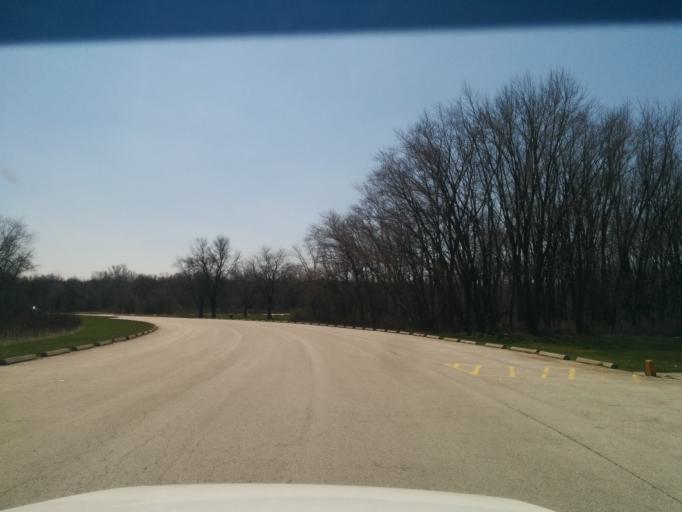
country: US
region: Illinois
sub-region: Cook County
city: Midlothian
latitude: 41.6116
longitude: -87.7234
